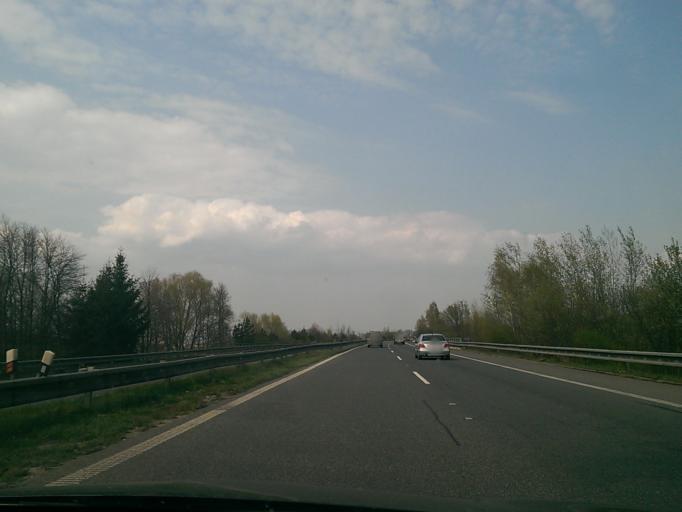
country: CZ
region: Central Bohemia
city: Mnichovo Hradiste
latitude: 50.4993
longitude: 14.9759
